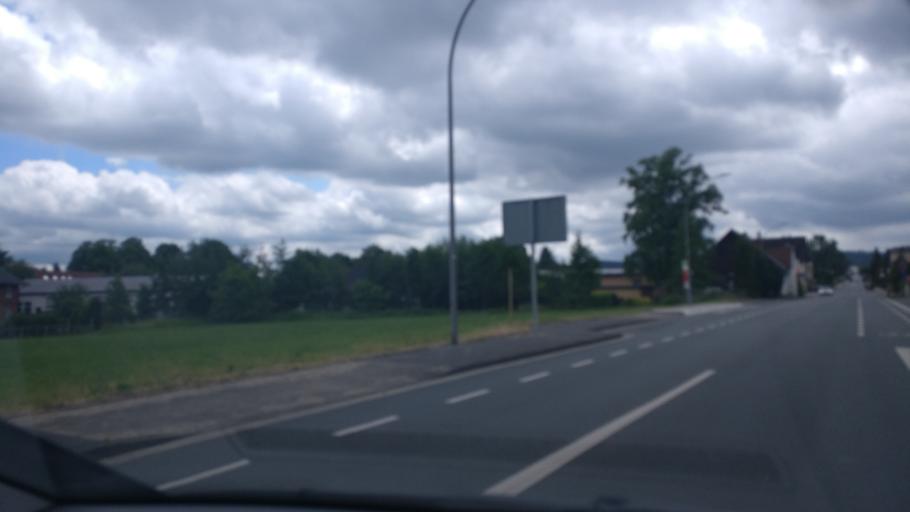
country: DE
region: North Rhine-Westphalia
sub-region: Regierungsbezirk Detmold
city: Leopoldshohe
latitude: 51.9812
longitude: 8.7143
